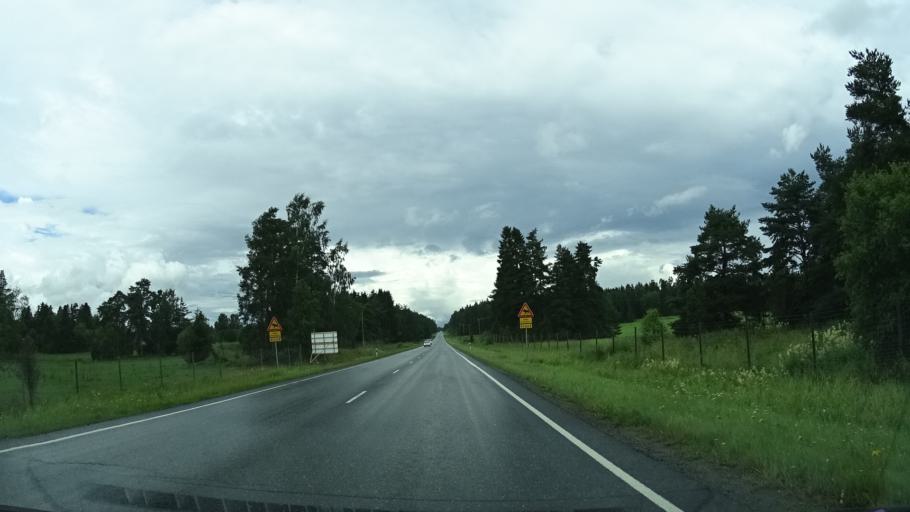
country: FI
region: Haeme
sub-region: Haemeenlinna
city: Kalvola
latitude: 61.1492
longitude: 24.0576
